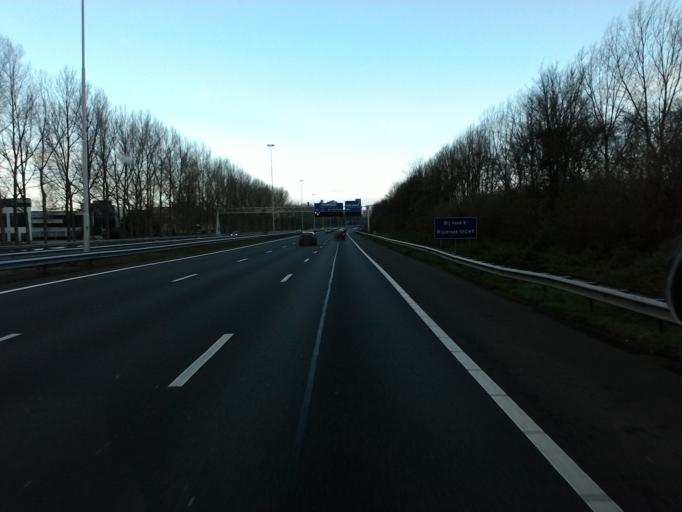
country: NL
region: South Holland
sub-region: Gemeente Capelle aan den IJssel
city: Capelle aan den IJssel
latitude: 51.9610
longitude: 4.5757
